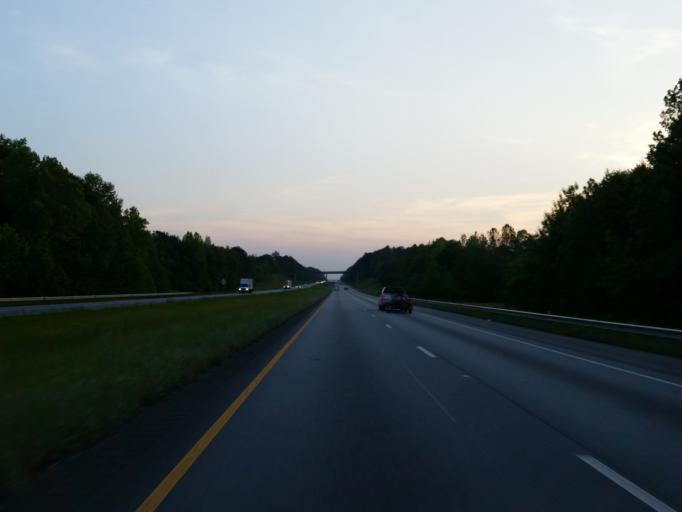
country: US
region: Alabama
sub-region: Cleburne County
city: Heflin
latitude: 33.6366
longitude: -85.5319
